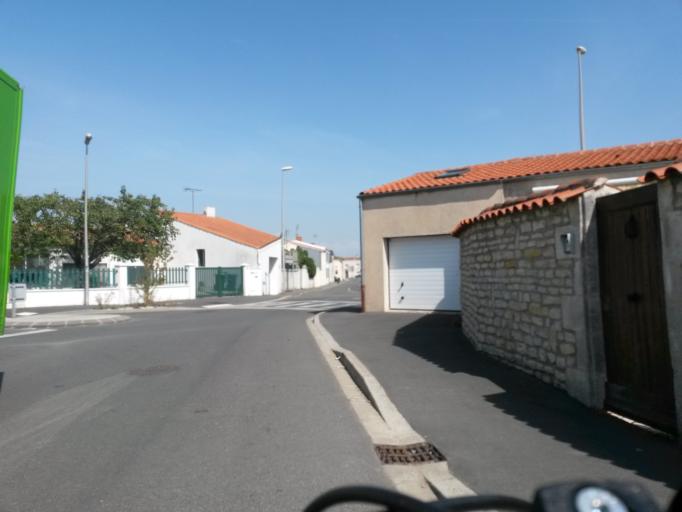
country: FR
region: Poitou-Charentes
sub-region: Departement de la Charente-Maritime
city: Saint-Xandre
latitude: 46.2019
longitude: -1.1050
